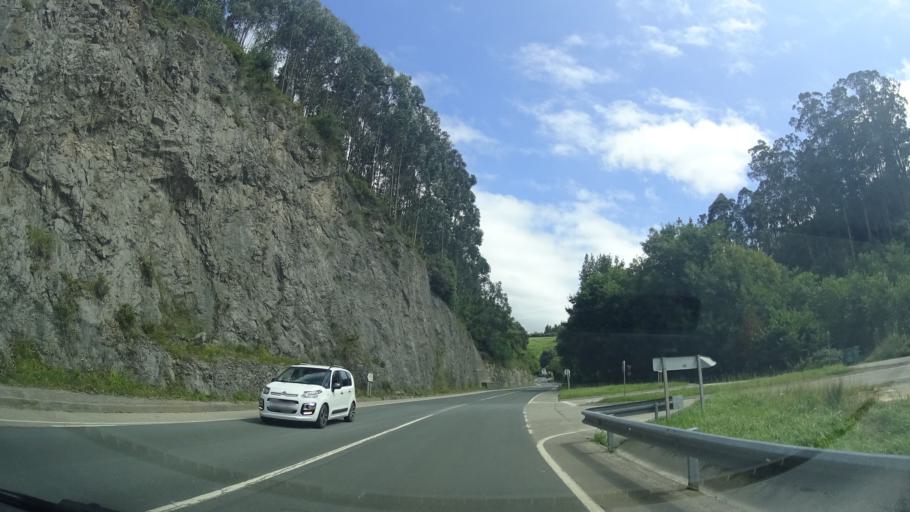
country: ES
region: Asturias
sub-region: Province of Asturias
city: Ribadesella
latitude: 43.4670
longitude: -5.1304
